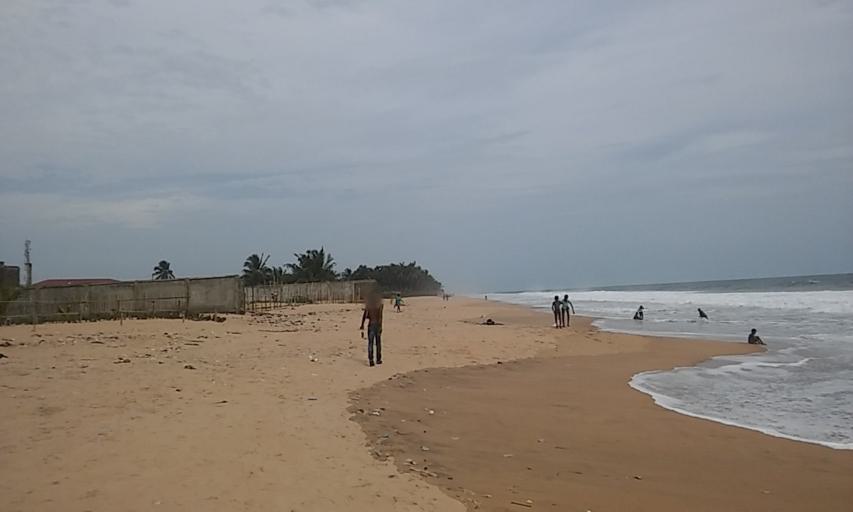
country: CI
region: Sud-Comoe
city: Grand-Bassam
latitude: 5.1933
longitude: -3.7320
